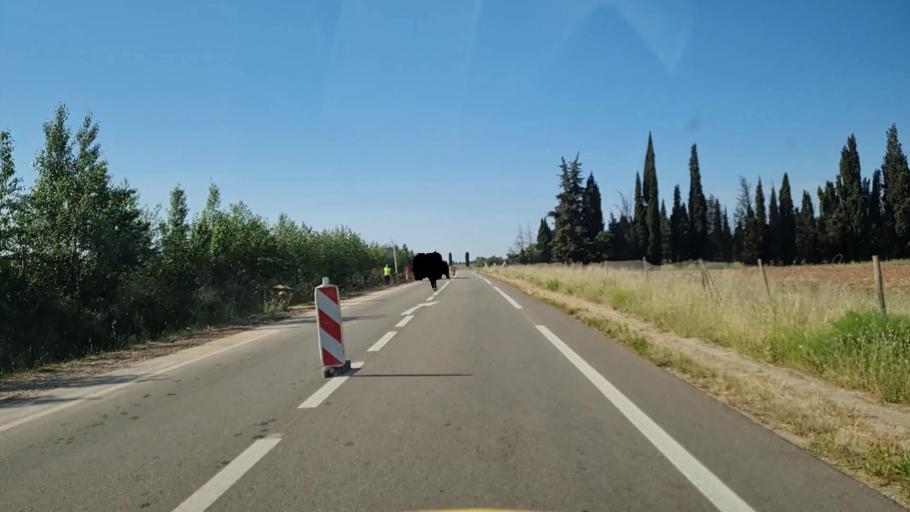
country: FR
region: Languedoc-Roussillon
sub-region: Departement du Gard
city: Garons
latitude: 43.7426
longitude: 4.4088
